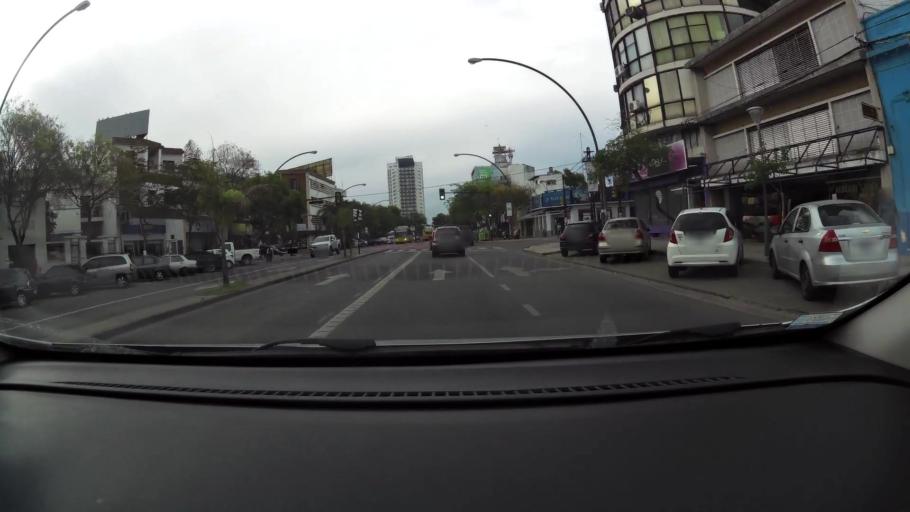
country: AR
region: Santa Fe
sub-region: Departamento de Rosario
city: Rosario
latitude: -32.9166
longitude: -60.6845
